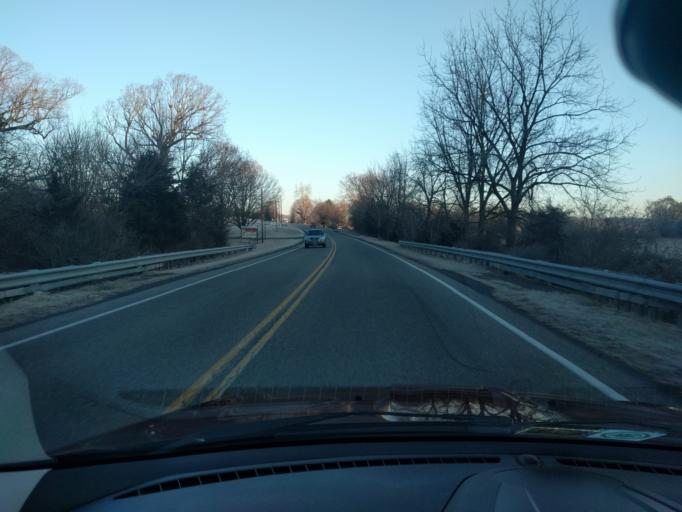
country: US
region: Virginia
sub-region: Augusta County
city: Weyers Cave
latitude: 38.3003
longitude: -78.9342
